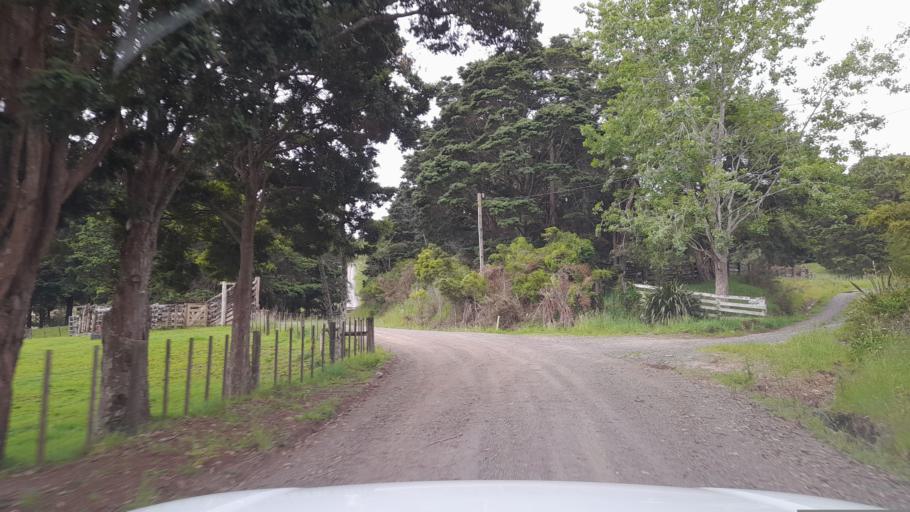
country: NZ
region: Northland
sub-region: Far North District
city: Waimate North
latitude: -35.3952
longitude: 173.7839
